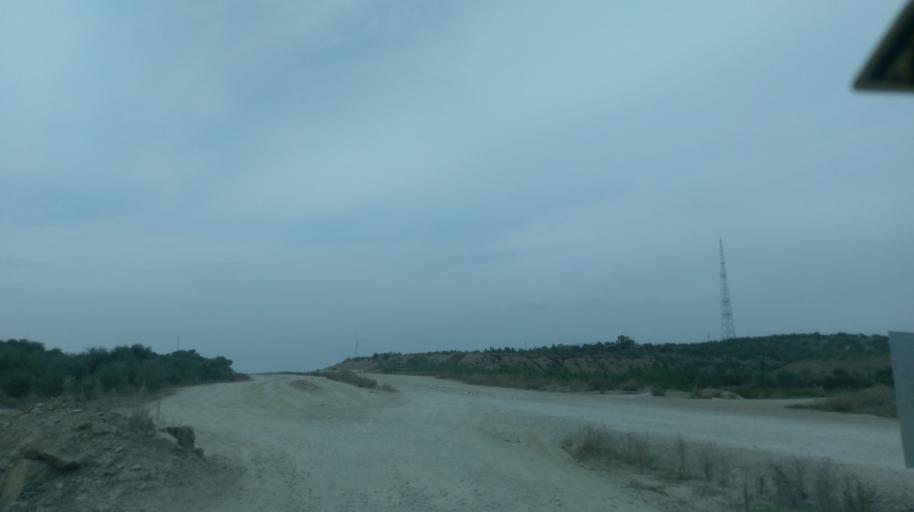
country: CY
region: Lefkosia
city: Nicosia
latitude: 35.2359
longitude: 33.3315
